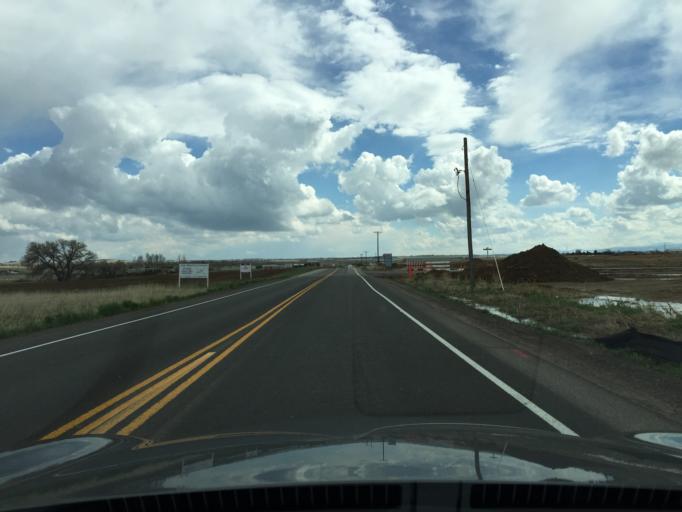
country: US
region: Colorado
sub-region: Boulder County
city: Erie
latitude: 40.0190
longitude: -105.0553
